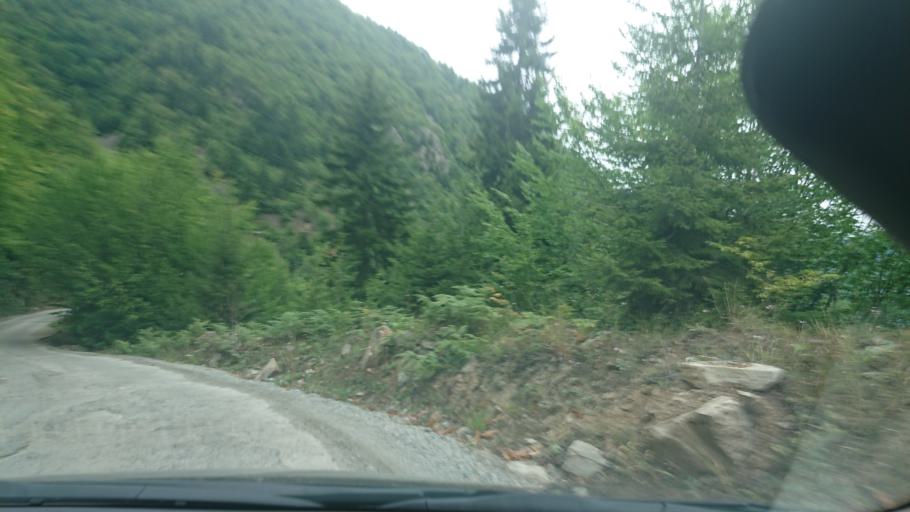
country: TR
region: Gumushane
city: Kurtun
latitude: 40.6854
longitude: 39.0506
